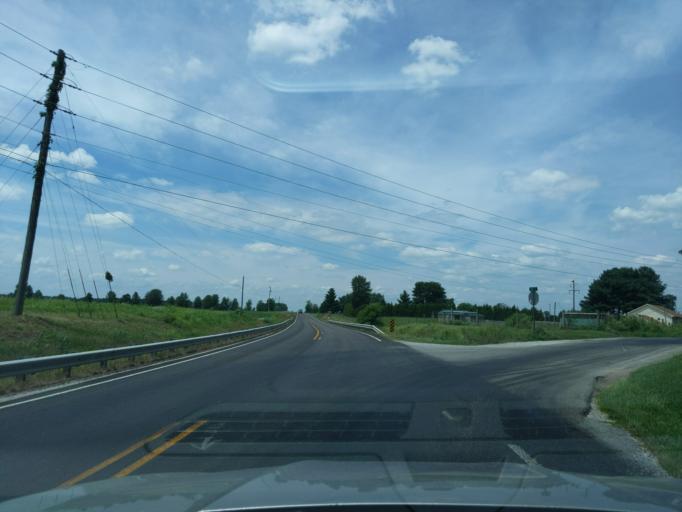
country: US
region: Indiana
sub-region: Ripley County
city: Osgood
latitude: 39.2433
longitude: -85.3474
